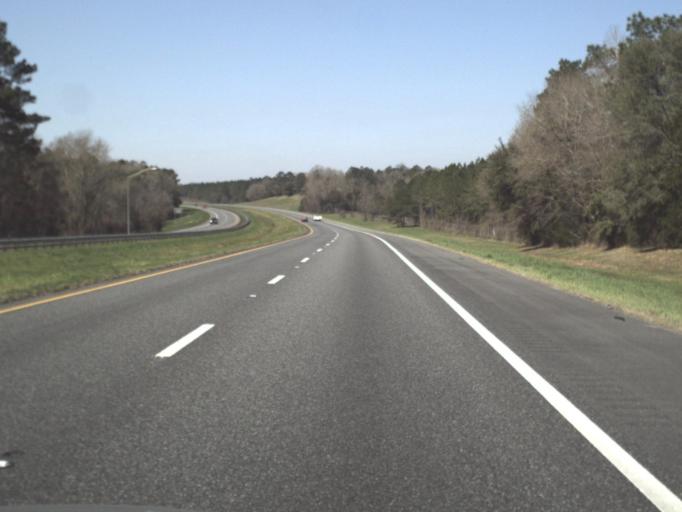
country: US
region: Florida
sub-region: Jackson County
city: Marianna
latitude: 30.7575
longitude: -85.3318
